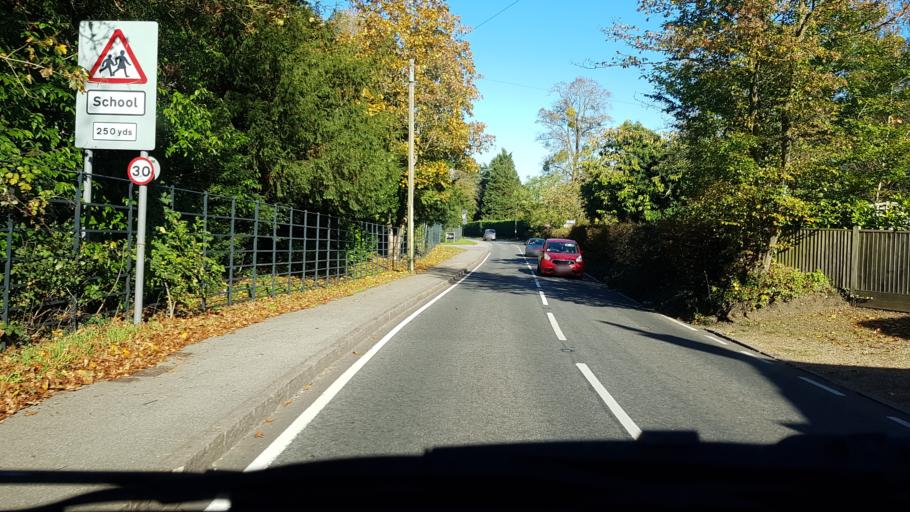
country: GB
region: England
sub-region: Surrey
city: Send
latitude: 51.2513
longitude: -0.5049
